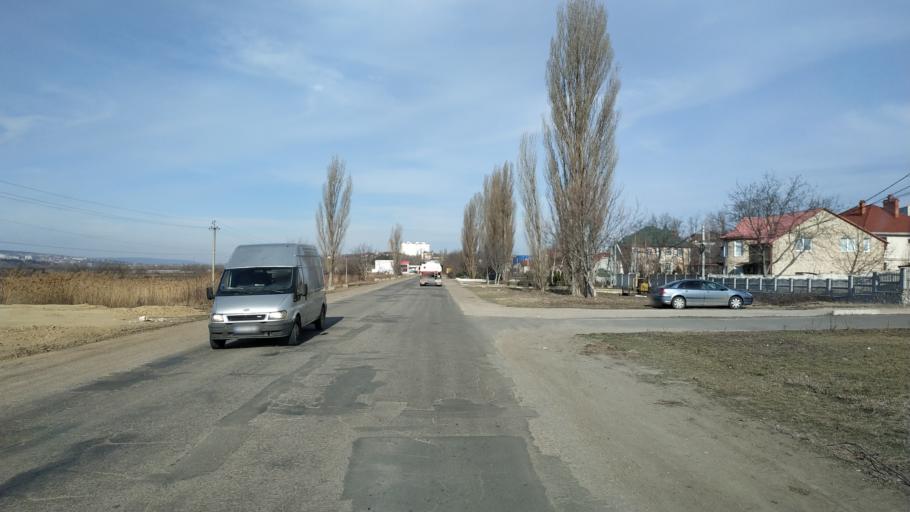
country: MD
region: Laloveni
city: Ialoveni
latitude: 46.9469
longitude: 28.7709
